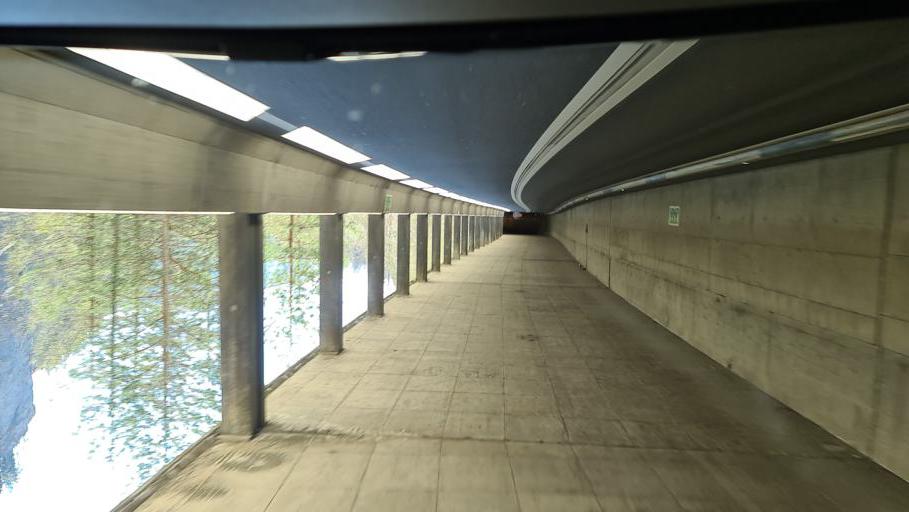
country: CH
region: Grisons
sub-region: Hinterrhein District
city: Thusis
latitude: 46.6481
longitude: 9.4483
